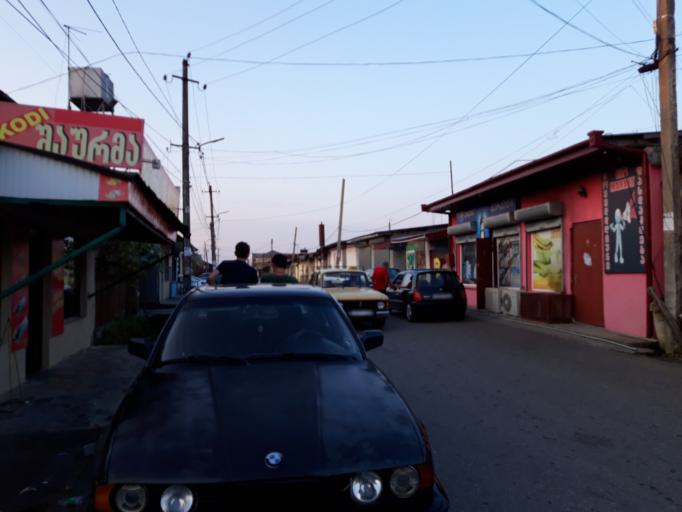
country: GE
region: Imereti
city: Samtredia
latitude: 42.1655
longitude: 42.3402
